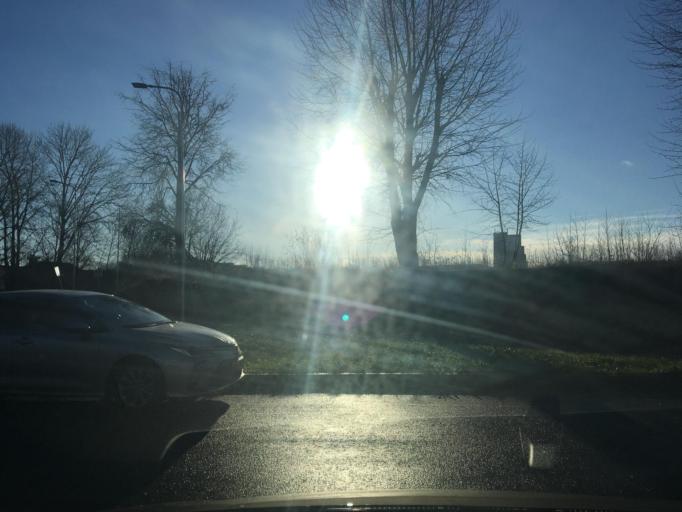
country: EE
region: Ida-Virumaa
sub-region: Narva linn
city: Narva
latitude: 59.3842
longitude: 28.1713
